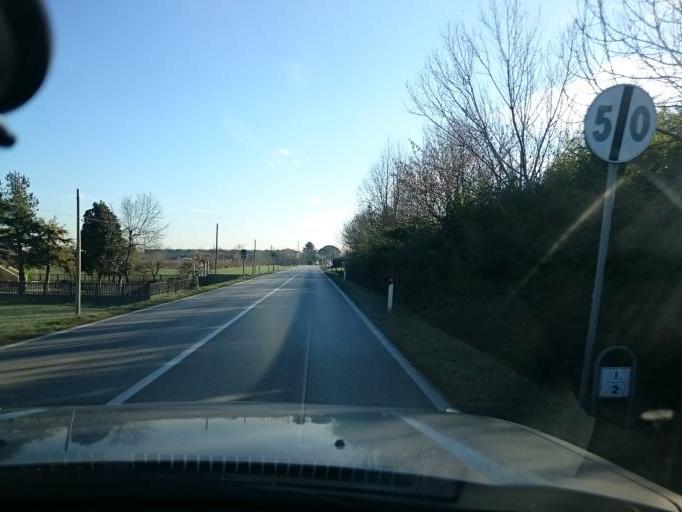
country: IT
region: Veneto
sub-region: Provincia di Padova
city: Terradura
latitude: 45.3228
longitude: 11.8351
